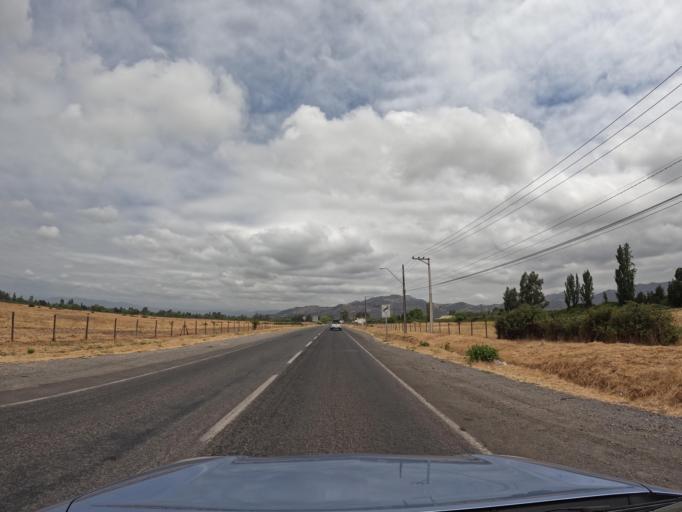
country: CL
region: Maule
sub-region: Provincia de Curico
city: Teno
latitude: -34.8642
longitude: -71.1754
